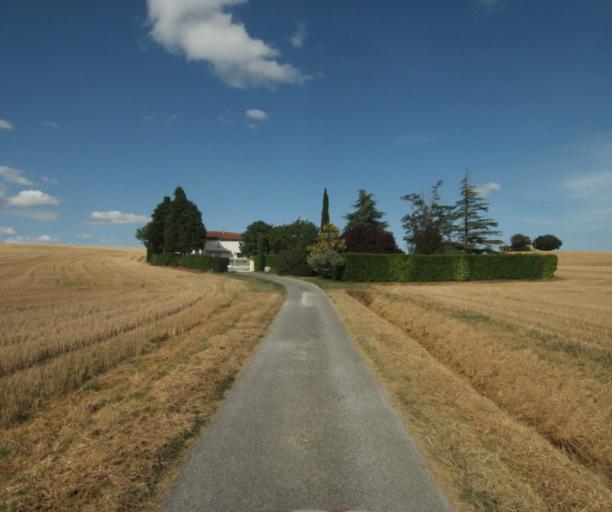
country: FR
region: Midi-Pyrenees
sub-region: Departement du Tarn
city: Puylaurens
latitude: 43.5296
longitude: 1.9983
